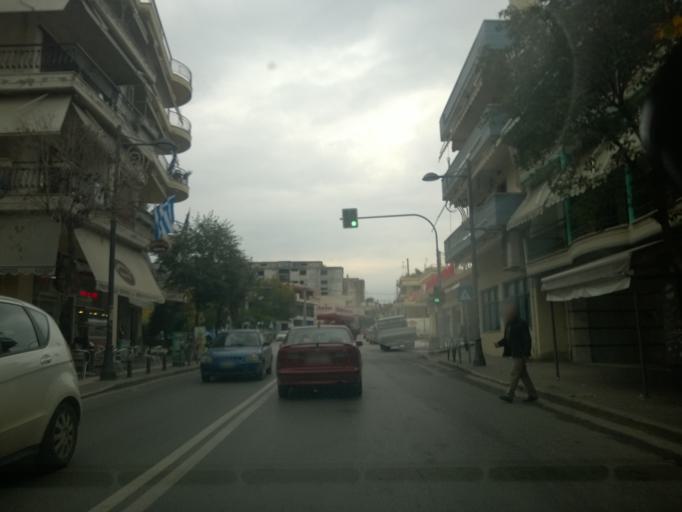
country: GR
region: Central Macedonia
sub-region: Nomos Thessalonikis
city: Stavroupoli
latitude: 40.6727
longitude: 22.9340
